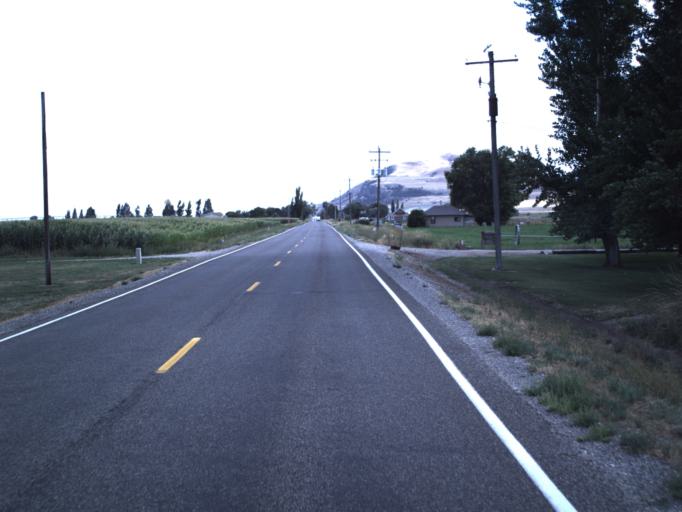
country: US
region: Utah
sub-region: Cache County
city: Lewiston
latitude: 41.9468
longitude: -111.9539
